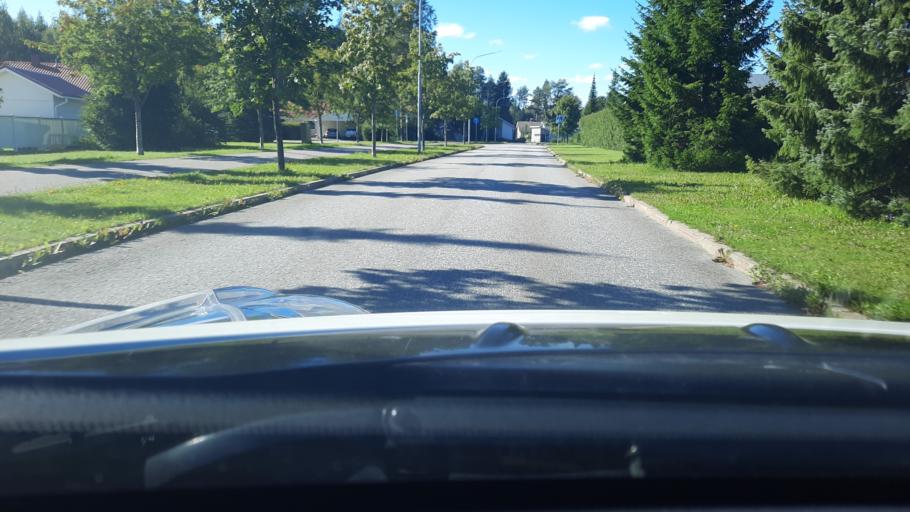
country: FI
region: North Karelia
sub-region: Joensuu
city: Joensuu
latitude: 62.6346
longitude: 29.6868
